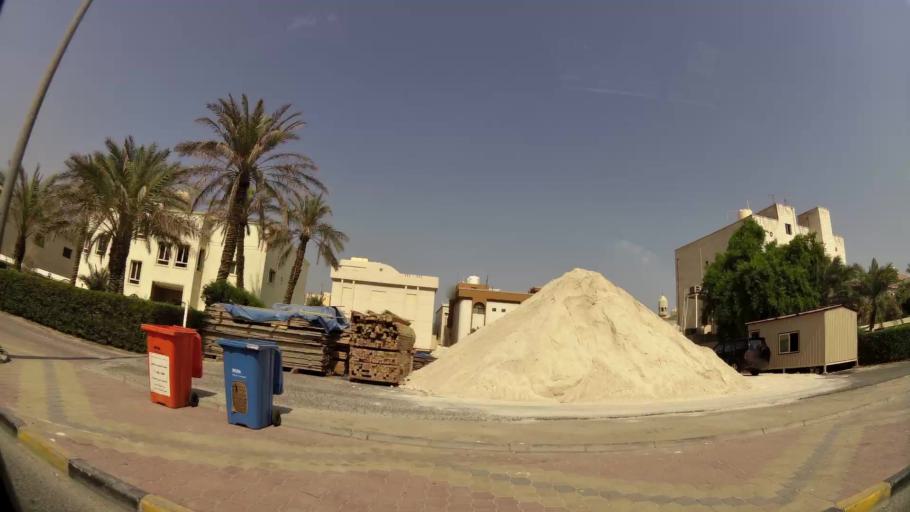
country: KW
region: Al Asimah
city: Ash Shamiyah
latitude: 29.3342
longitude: 47.9546
